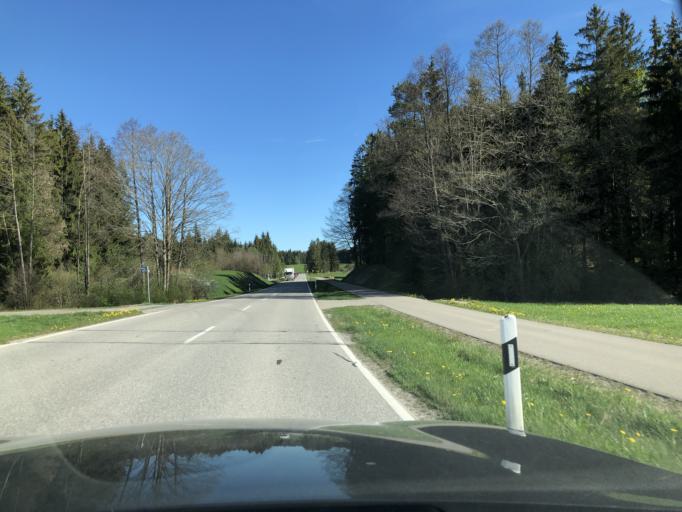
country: DE
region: Bavaria
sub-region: Swabia
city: Ruckholz
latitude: 47.6688
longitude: 10.5409
